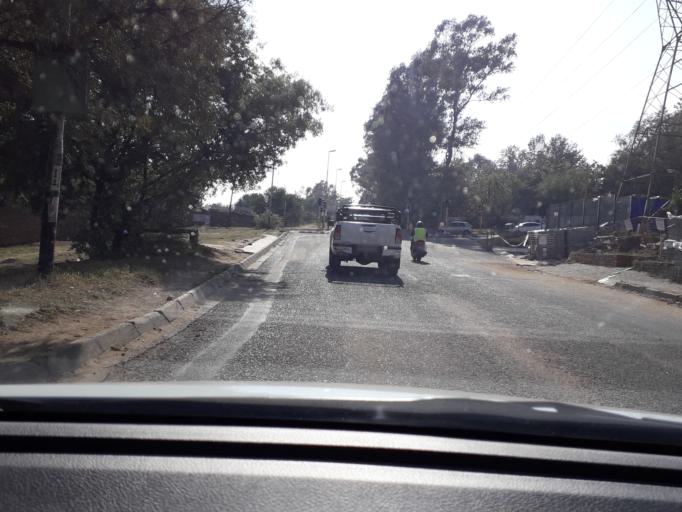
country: ZA
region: Gauteng
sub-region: City of Johannesburg Metropolitan Municipality
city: Roodepoort
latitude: -26.0779
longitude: 27.9623
